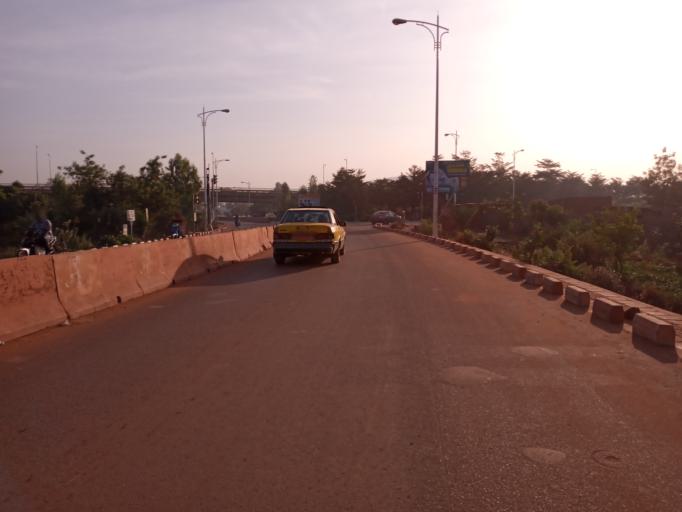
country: ML
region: Bamako
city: Bamako
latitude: 12.6359
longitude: -7.9248
